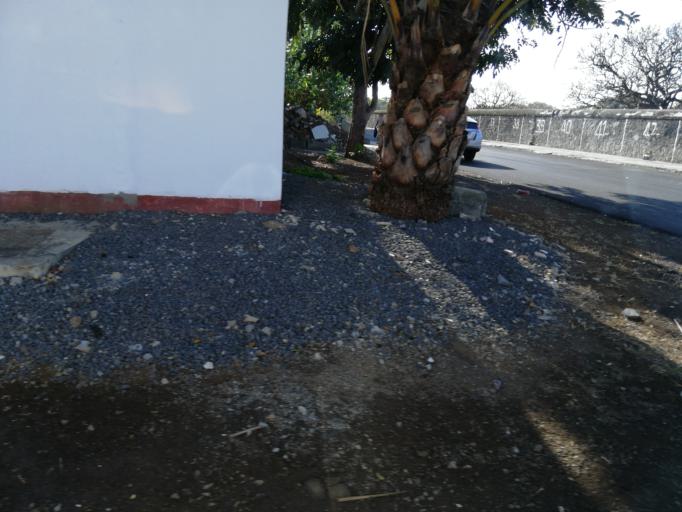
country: MU
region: Port Louis
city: Port Louis
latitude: -20.1617
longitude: 57.4883
